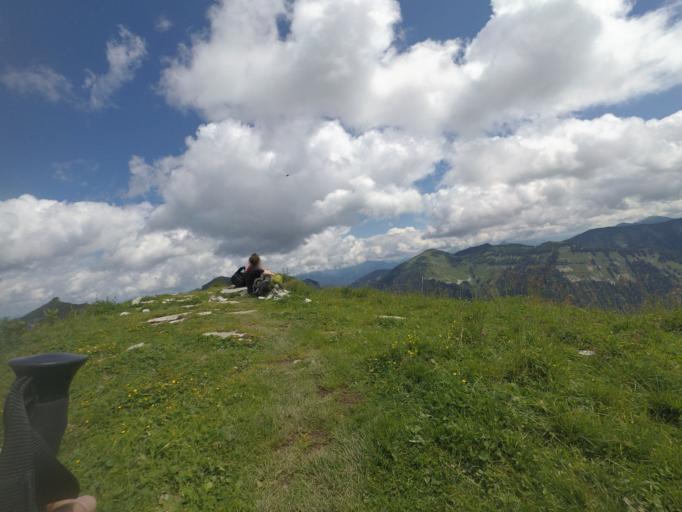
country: AT
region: Salzburg
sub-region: Politischer Bezirk Salzburg-Umgebung
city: Hintersee
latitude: 47.6604
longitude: 13.2942
